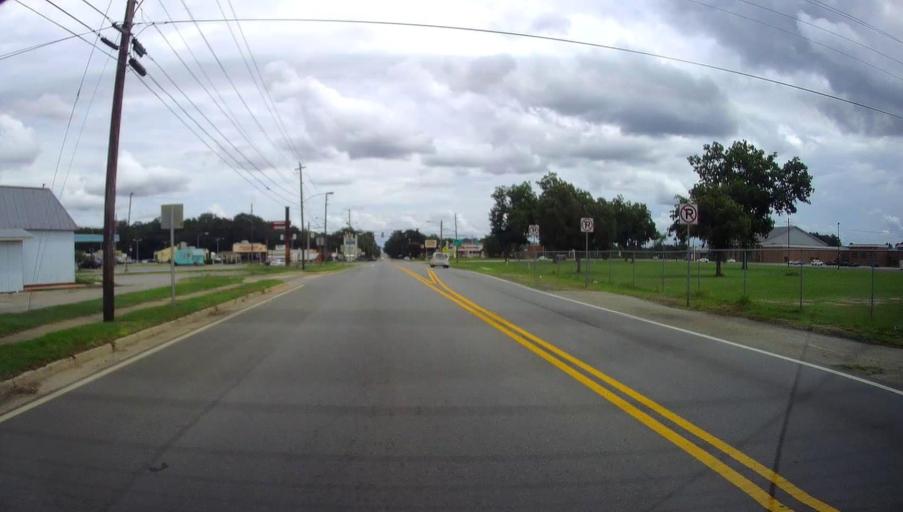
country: US
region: Georgia
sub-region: Macon County
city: Montezuma
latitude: 32.2936
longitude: -84.0211
